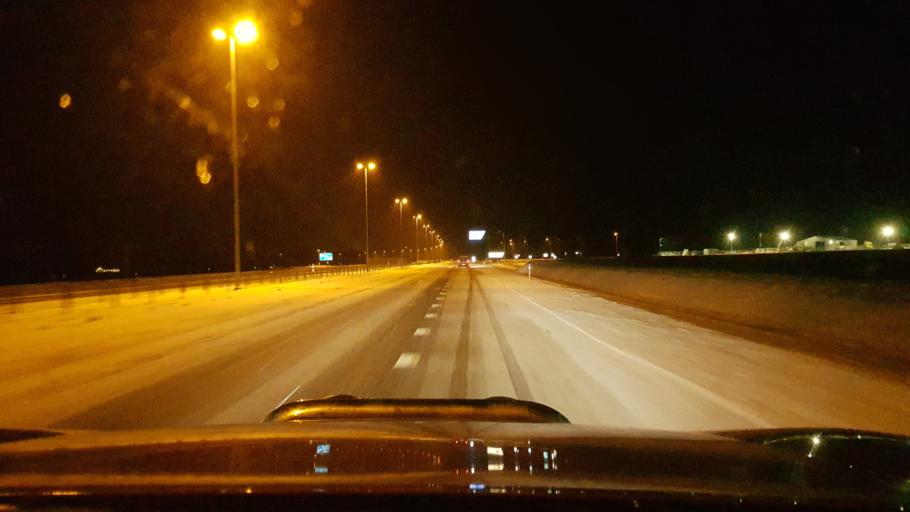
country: EE
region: Harju
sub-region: Rae vald
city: Vaida
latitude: 59.2029
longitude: 25.0401
